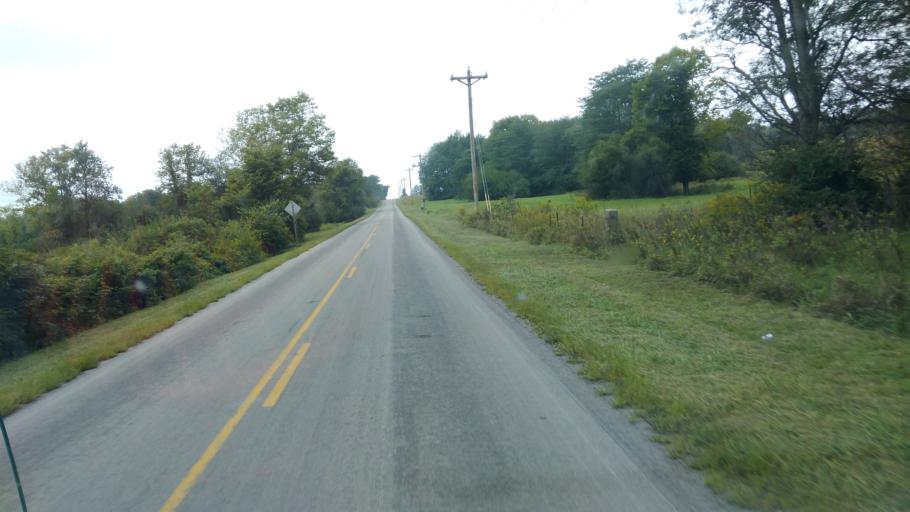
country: US
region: Ohio
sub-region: Hardin County
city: Kenton
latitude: 40.5738
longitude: -83.6354
